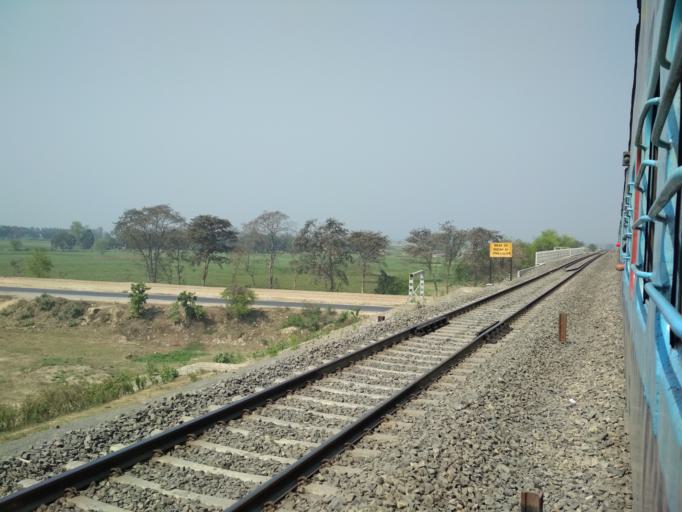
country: IN
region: Bihar
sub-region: Munger
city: Munger
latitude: 25.4373
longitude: 86.4340
